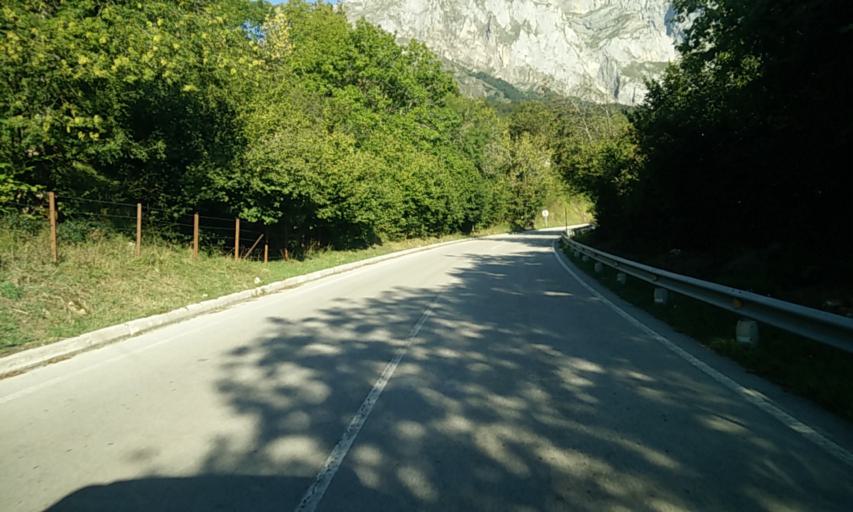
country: ES
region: Castille and Leon
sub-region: Provincia de Leon
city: Posada de Valdeon
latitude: 43.1314
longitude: -4.8076
